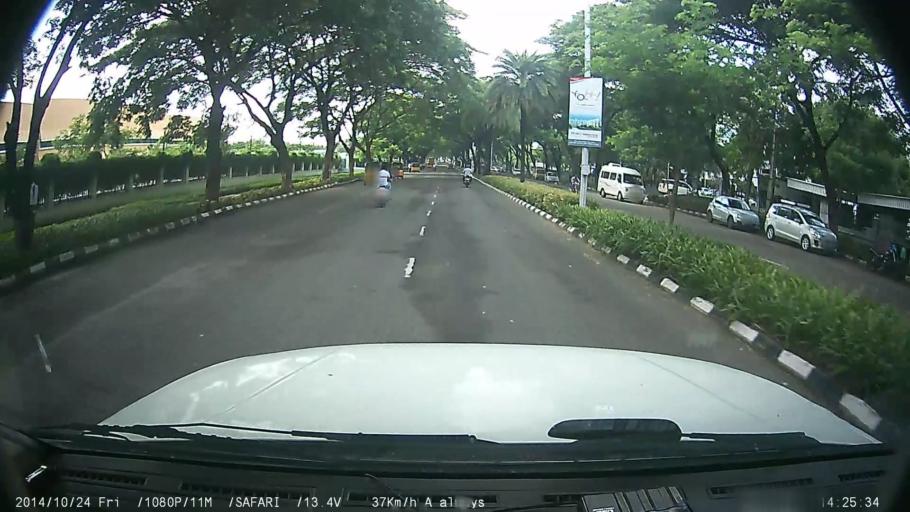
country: IN
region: Tamil Nadu
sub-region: Kancheepuram
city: Singapperumalkovil
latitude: 12.7367
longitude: 80.0058
